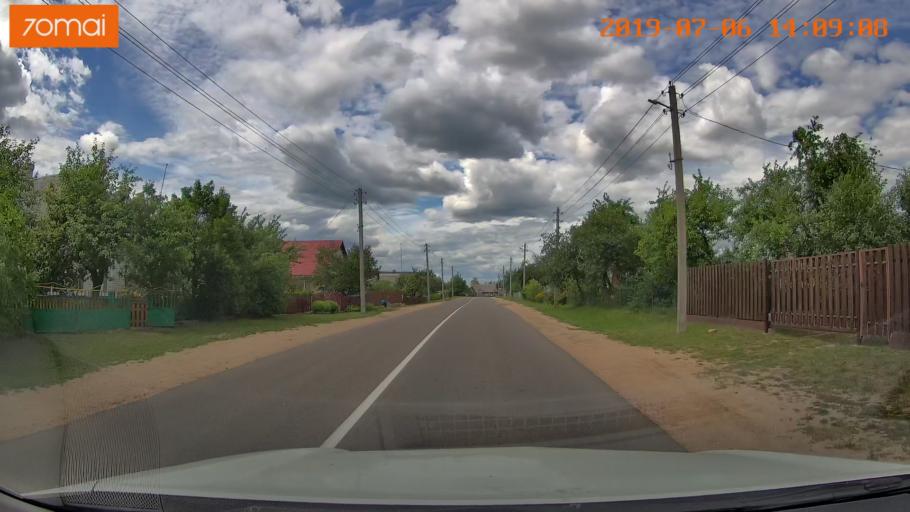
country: BY
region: Minsk
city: Ivyanyets
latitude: 53.8795
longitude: 26.7505
